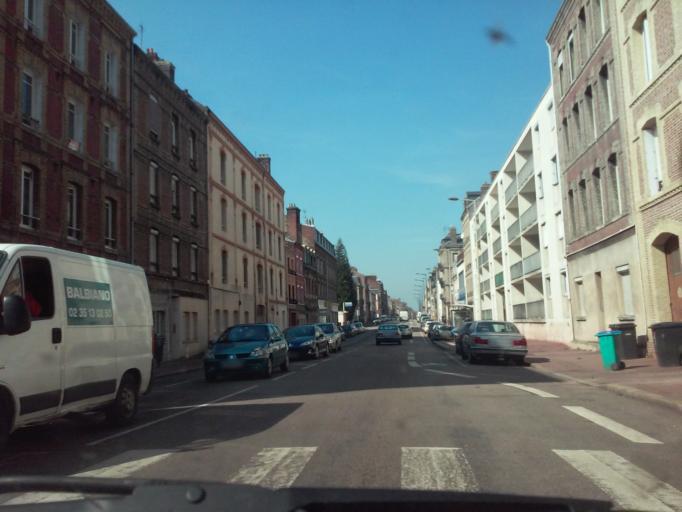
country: FR
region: Haute-Normandie
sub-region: Departement de la Seine-Maritime
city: Fontaine-la-Mallet
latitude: 49.5015
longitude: 0.1500
